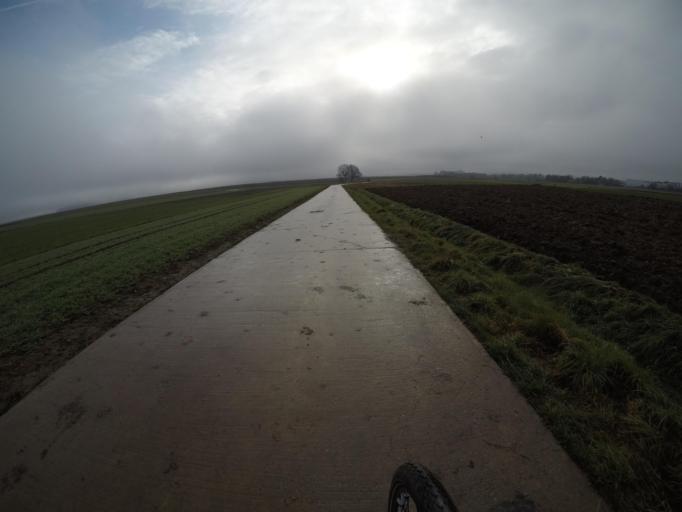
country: DE
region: Baden-Wuerttemberg
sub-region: Regierungsbezirk Stuttgart
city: Wolfschlugen
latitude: 48.6510
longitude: 9.2592
